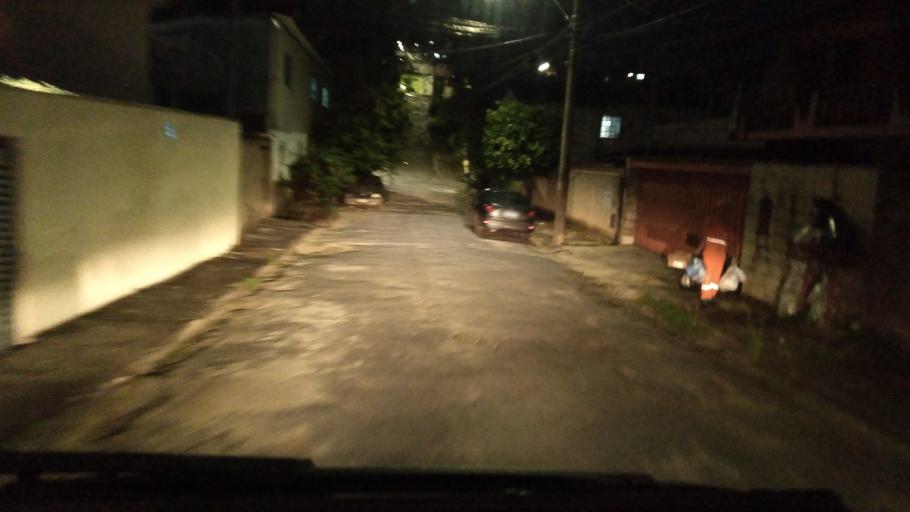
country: BR
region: Minas Gerais
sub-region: Belo Horizonte
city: Belo Horizonte
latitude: -19.9016
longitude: -43.9725
